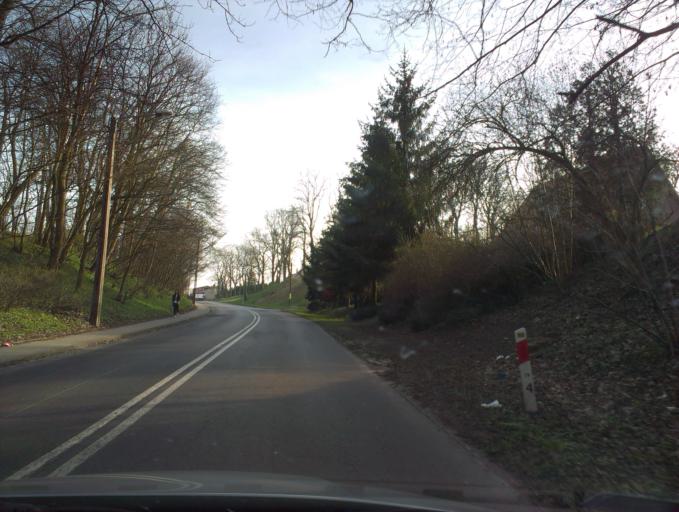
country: PL
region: Pomeranian Voivodeship
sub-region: Powiat czluchowski
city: Debrzno
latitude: 53.5314
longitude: 17.2307
